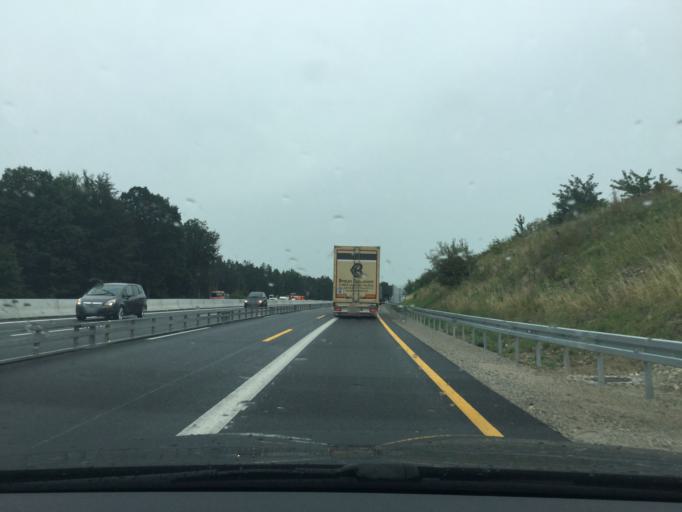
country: DE
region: Bavaria
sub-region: Upper Franconia
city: Haag
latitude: 49.8438
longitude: 11.5065
